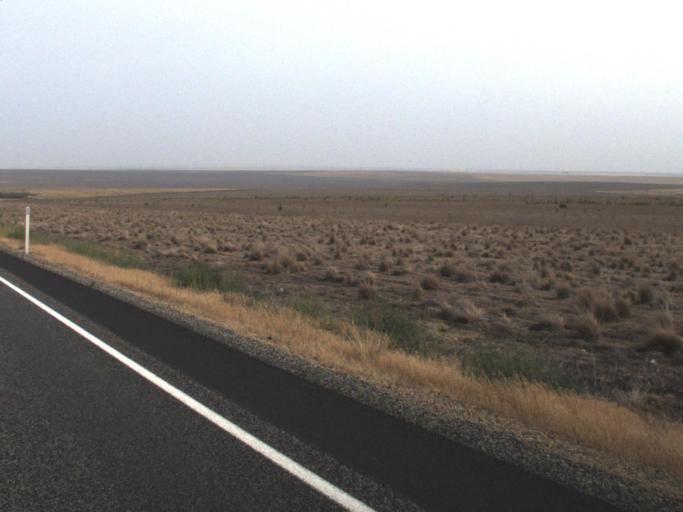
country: US
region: Washington
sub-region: Benton County
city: Prosser
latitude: 46.1873
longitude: -119.6964
